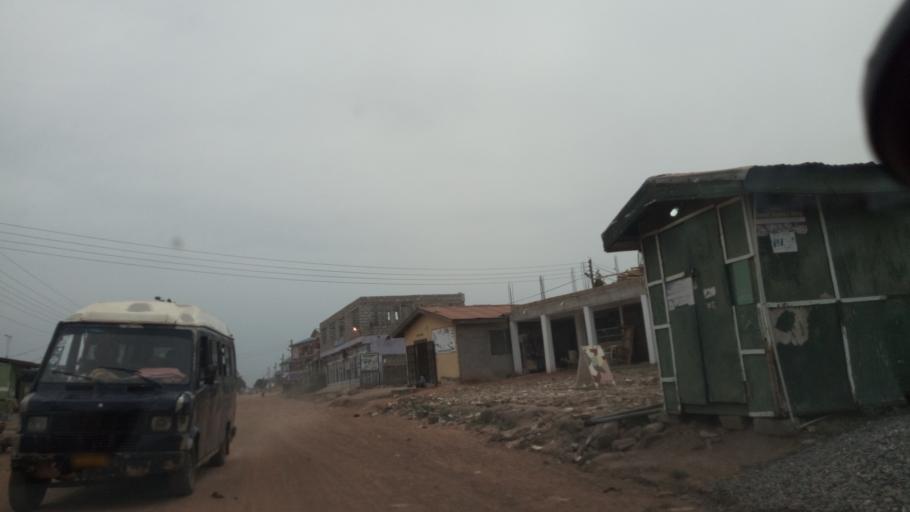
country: GH
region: Greater Accra
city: Medina Estates
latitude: 5.7080
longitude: -0.1314
